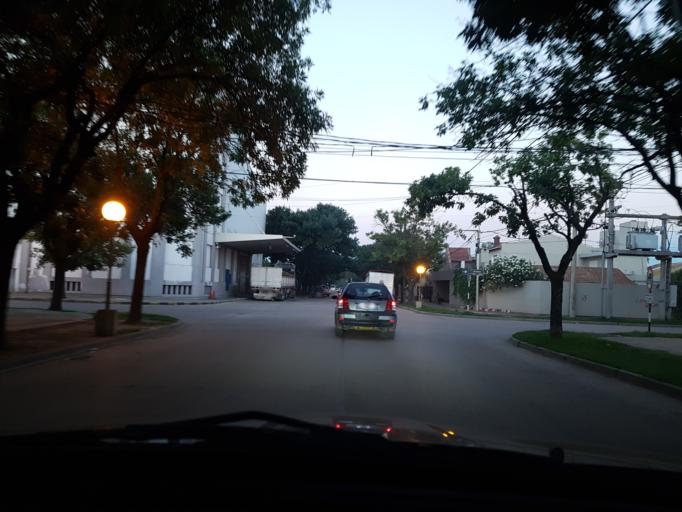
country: AR
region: Cordoba
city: General Cabrera
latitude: -32.7570
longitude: -63.7930
